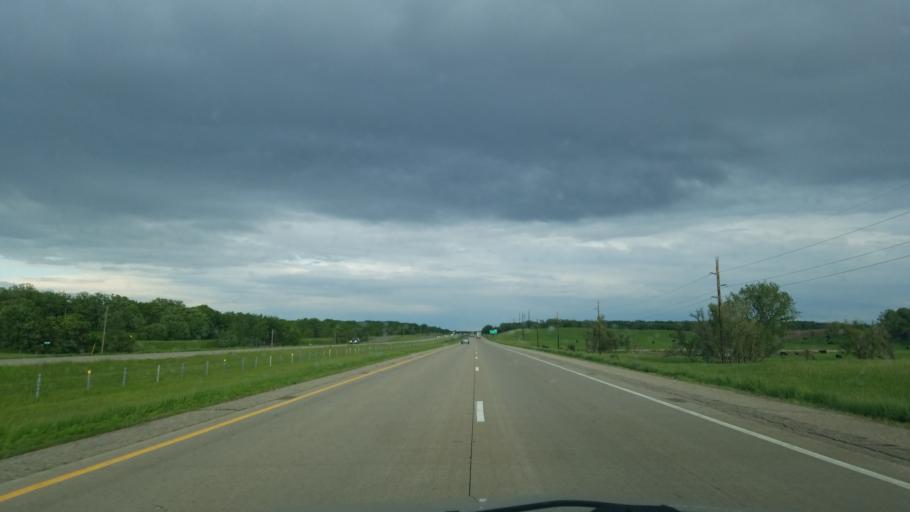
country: US
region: Minnesota
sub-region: Stearns County
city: Sauk Centre
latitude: 45.7591
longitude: -95.0177
